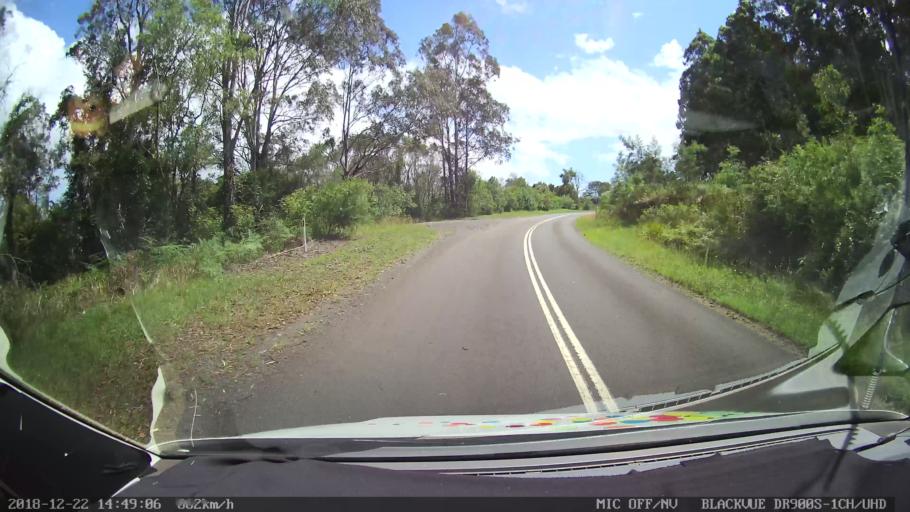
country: AU
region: New South Wales
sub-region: Bellingen
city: Dorrigo
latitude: -30.1869
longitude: 152.5508
